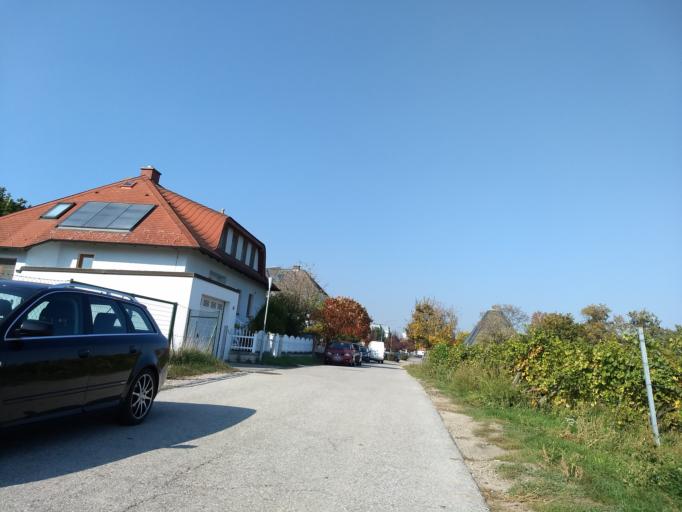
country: AT
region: Lower Austria
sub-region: Politischer Bezirk Modling
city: Perchtoldsdorf
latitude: 48.1154
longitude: 16.2750
